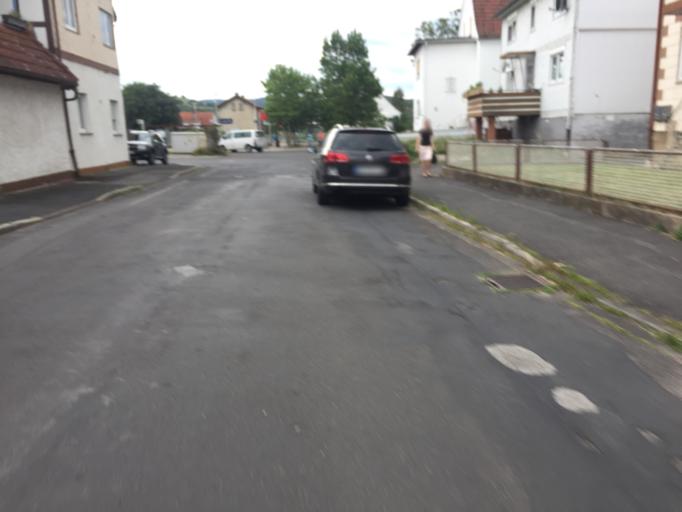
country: DE
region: Hesse
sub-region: Regierungsbezirk Kassel
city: Alheim
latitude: 51.0462
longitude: 9.6653
